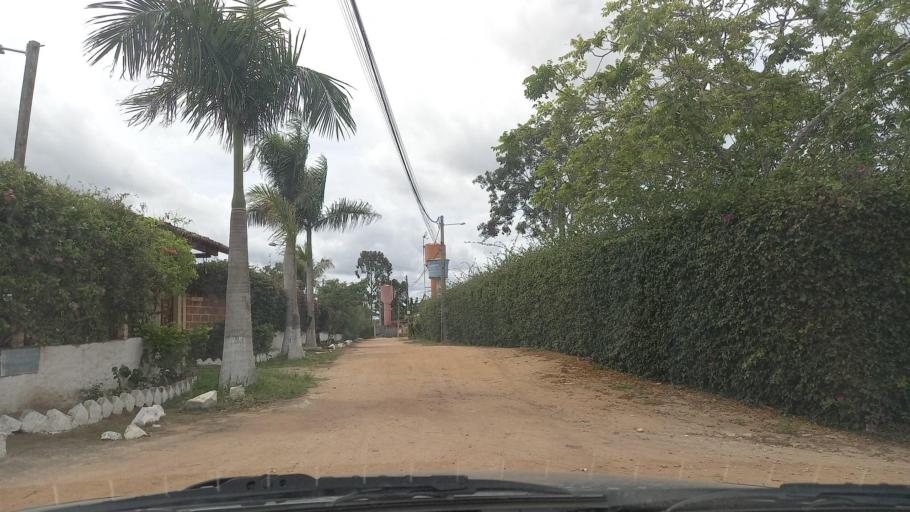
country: BR
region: Pernambuco
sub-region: Gravata
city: Gravata
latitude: -8.1922
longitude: -35.5912
